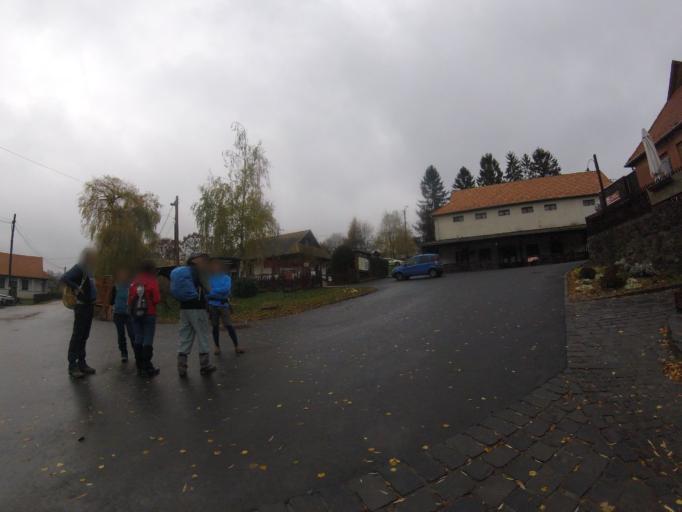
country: HU
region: Nograd
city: Rimoc
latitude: 47.9978
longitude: 19.5909
